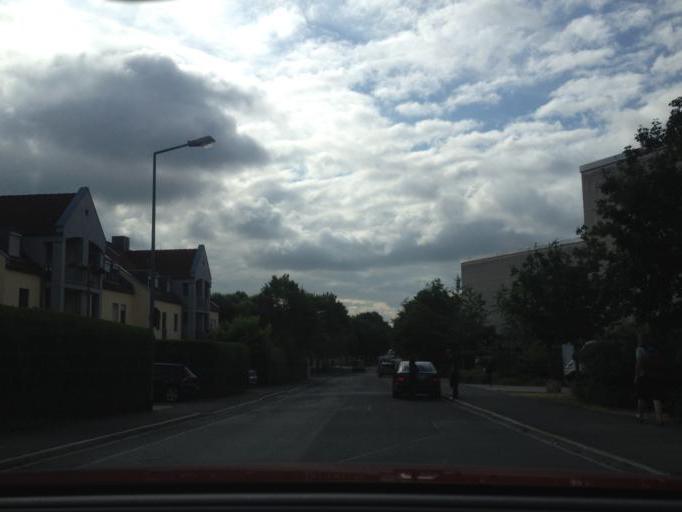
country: DE
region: Bavaria
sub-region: Regierungsbezirk Mittelfranken
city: Lauf an der Pegnitz
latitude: 49.5172
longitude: 11.2702
